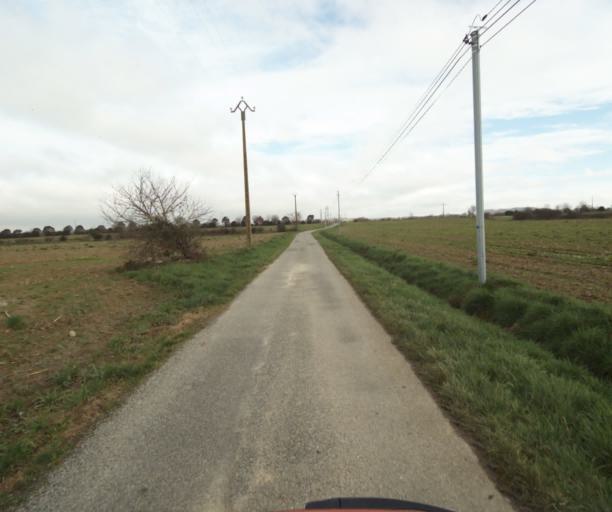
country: FR
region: Languedoc-Roussillon
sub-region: Departement de l'Aude
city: Belpech
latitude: 43.1600
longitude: 1.7060
